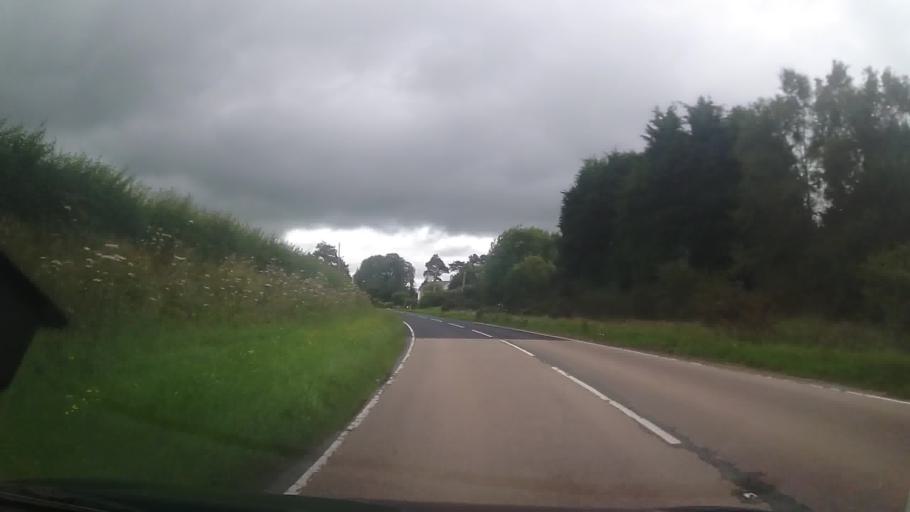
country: GB
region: England
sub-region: Shropshire
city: Whitchurch
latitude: 52.9617
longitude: -2.7333
